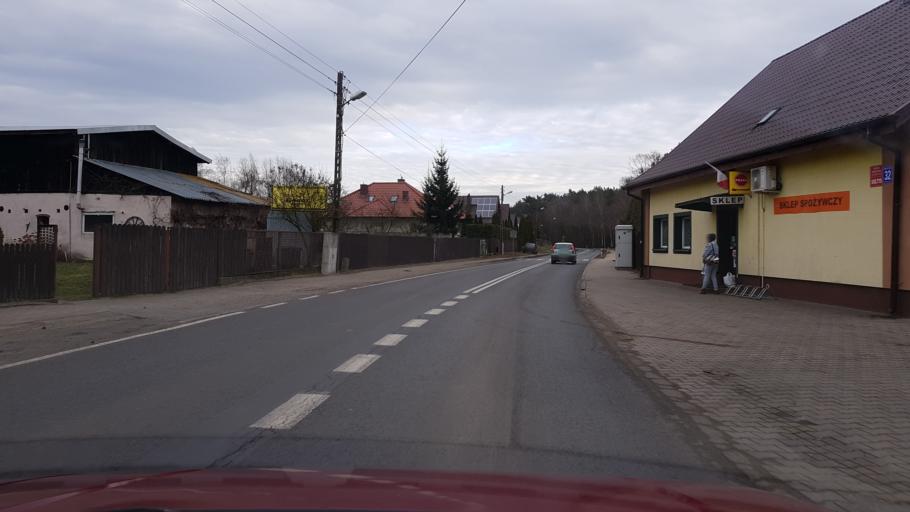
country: PL
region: West Pomeranian Voivodeship
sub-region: Powiat policki
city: Police
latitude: 53.5478
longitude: 14.5179
